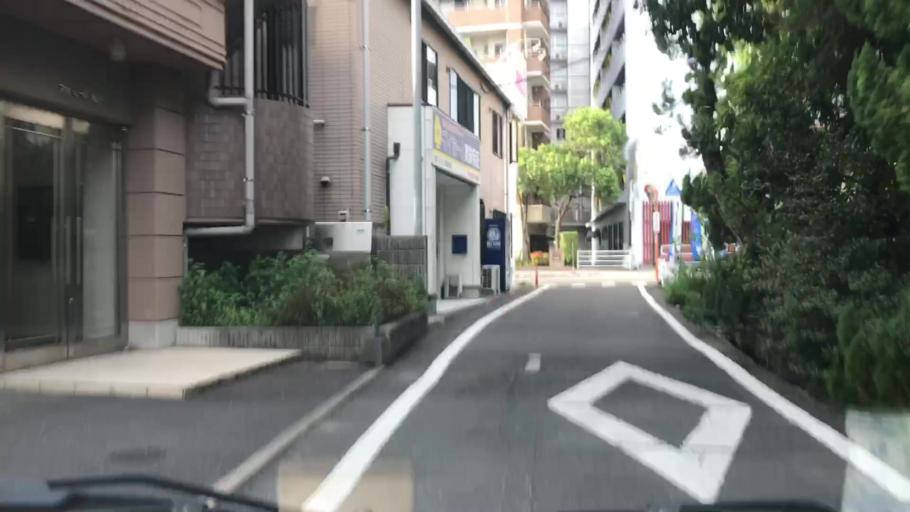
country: JP
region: Saga Prefecture
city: Saga-shi
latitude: 33.2612
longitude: 130.2972
